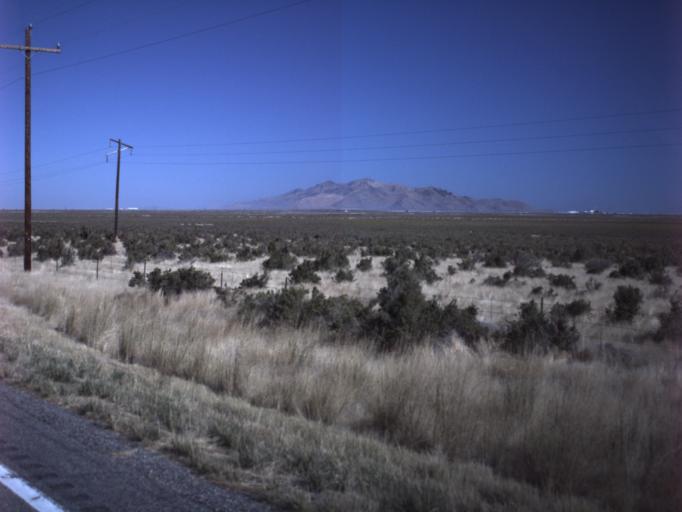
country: US
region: Utah
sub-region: Tooele County
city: Grantsville
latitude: 40.6590
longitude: -112.5380
